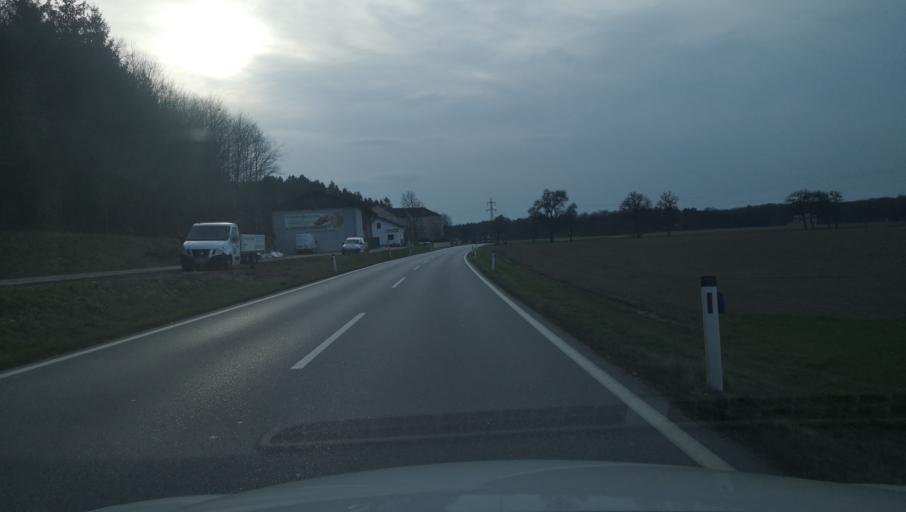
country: AT
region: Lower Austria
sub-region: Politischer Bezirk Amstetten
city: Amstetten
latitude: 48.1011
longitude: 14.8838
